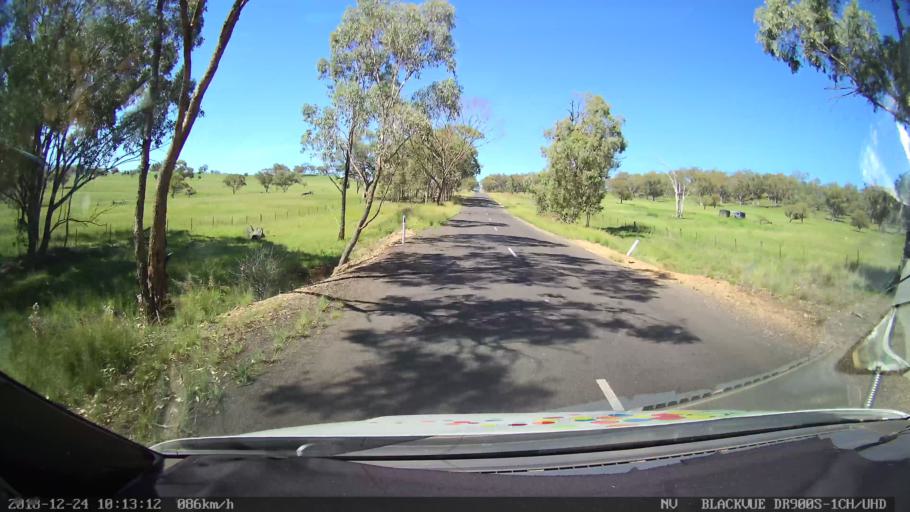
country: AU
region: New South Wales
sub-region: Liverpool Plains
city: Quirindi
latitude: -31.6872
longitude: 150.6415
